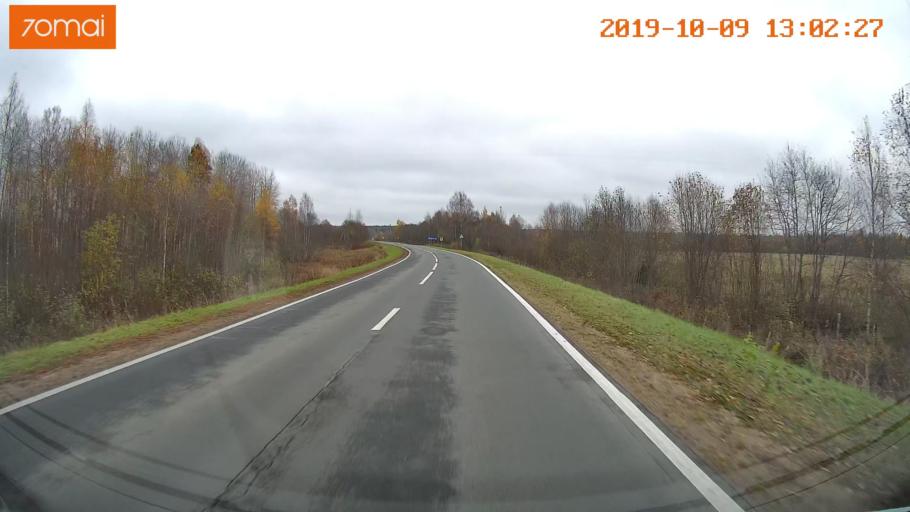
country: RU
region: Jaroslavl
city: Prechistoye
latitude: 58.3613
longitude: 40.5017
